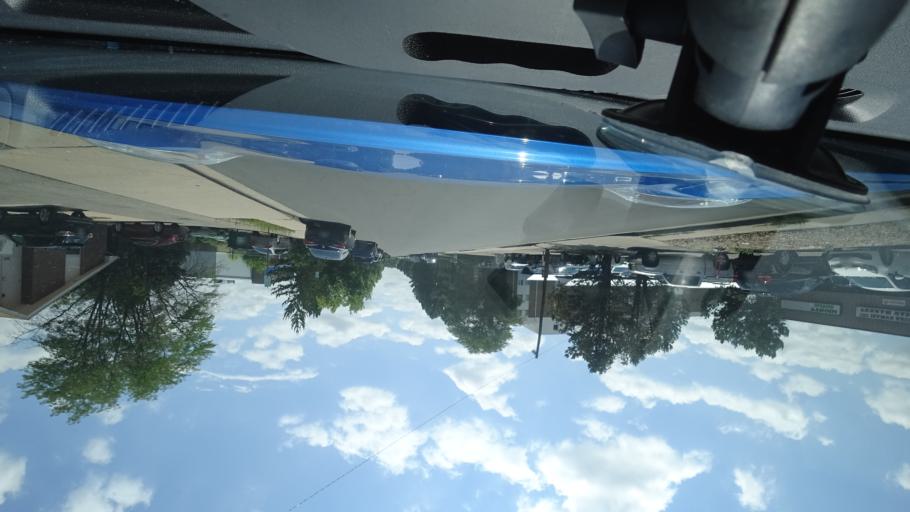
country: US
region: Colorado
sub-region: Adams County
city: Aurora
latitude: 39.7107
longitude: -104.8638
